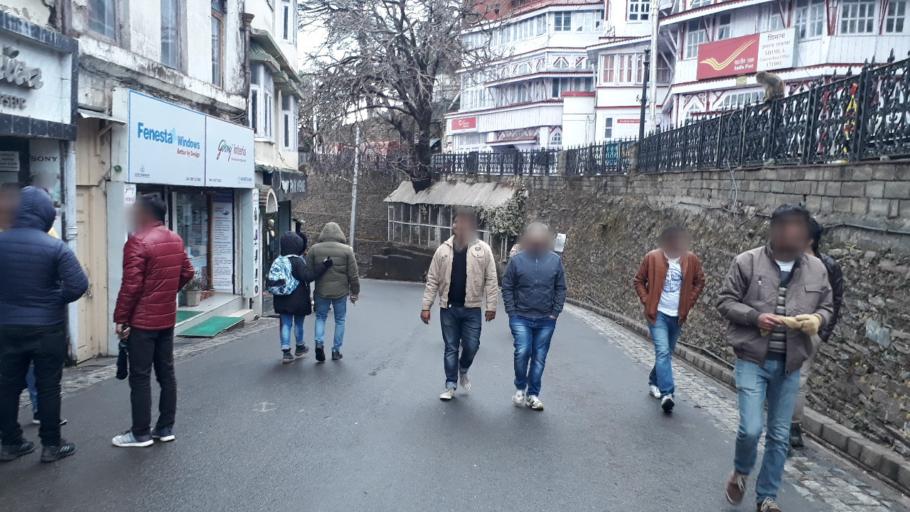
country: IN
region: Himachal Pradesh
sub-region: Shimla
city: Shimla
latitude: 31.1052
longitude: 77.1721
